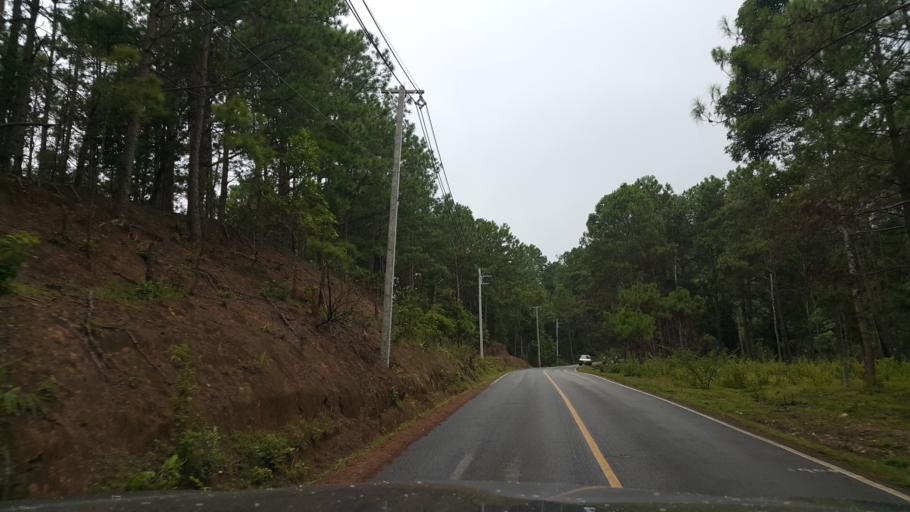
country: TH
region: Chiang Mai
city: Samoeng
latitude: 18.8856
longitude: 98.5274
